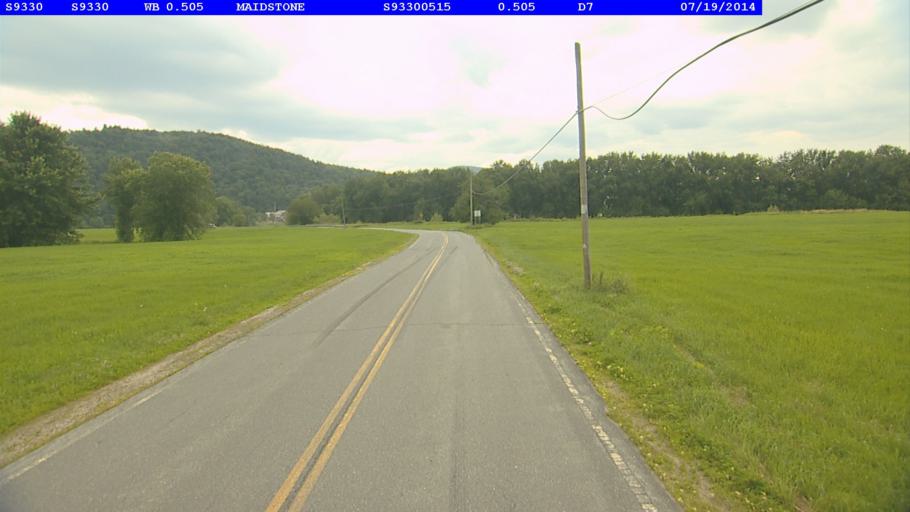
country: US
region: New Hampshire
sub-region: Coos County
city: Stratford
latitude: 44.6517
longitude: -71.5649
